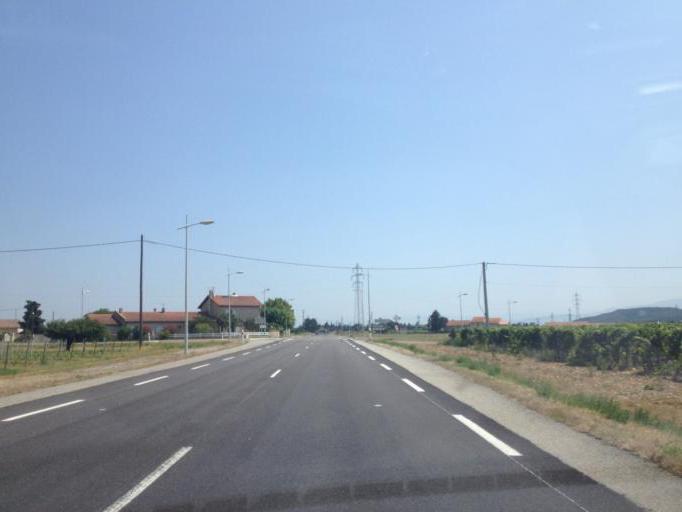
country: FR
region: Rhone-Alpes
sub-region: Departement de la Drome
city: Beaumont-Monteux
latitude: 45.0235
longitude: 4.9080
